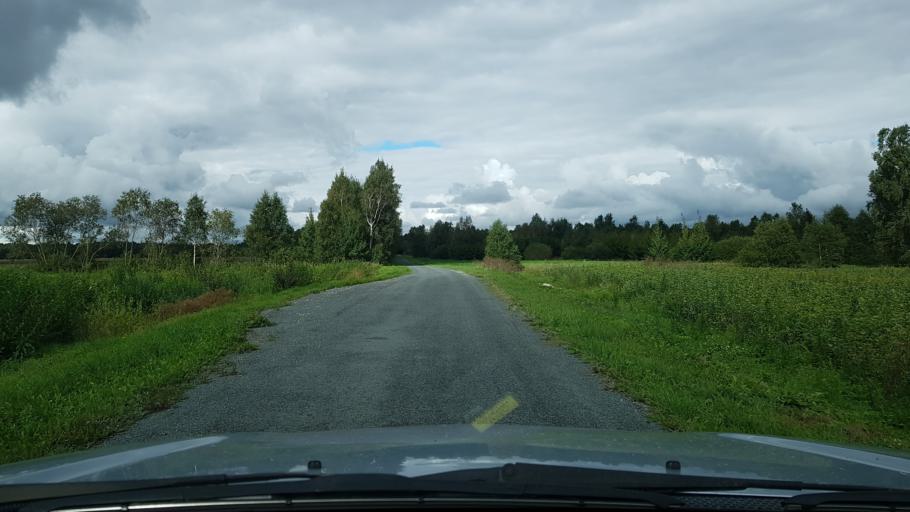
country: EE
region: Harju
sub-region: Raasiku vald
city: Arukula
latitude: 59.2829
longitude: 25.0727
